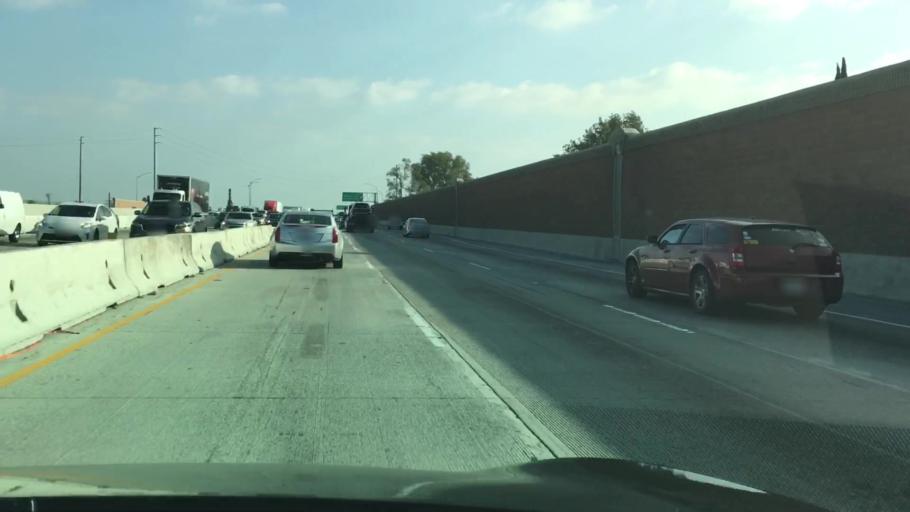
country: US
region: California
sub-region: Los Angeles County
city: Norwalk
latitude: 33.9232
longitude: -118.0845
